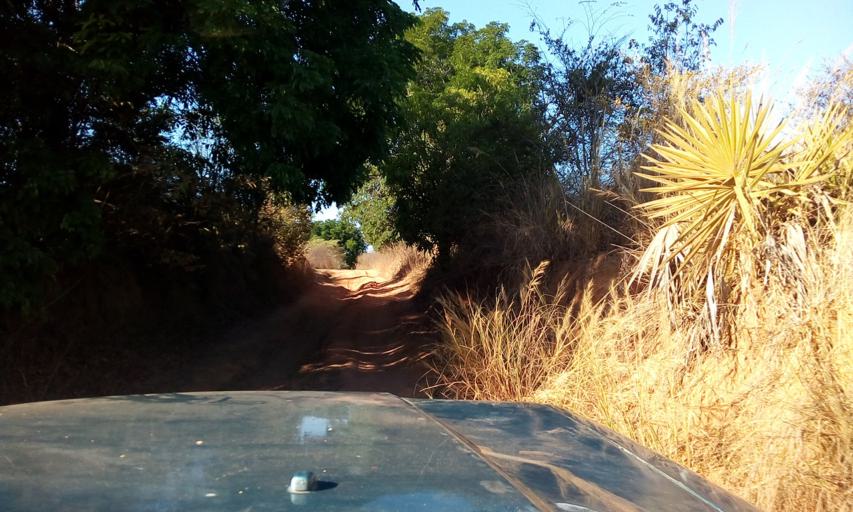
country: MG
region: Boeny
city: Sitampiky
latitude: -16.1741
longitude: 45.3610
